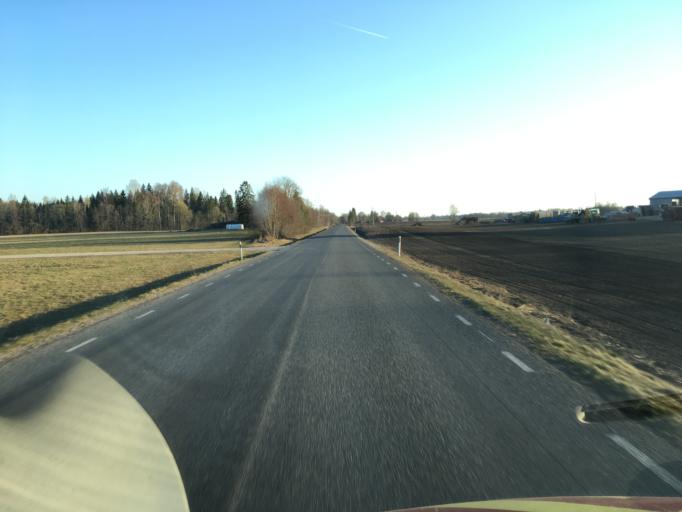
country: EE
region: Raplamaa
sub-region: Kehtna vald
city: Kehtna
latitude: 59.0504
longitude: 24.9488
